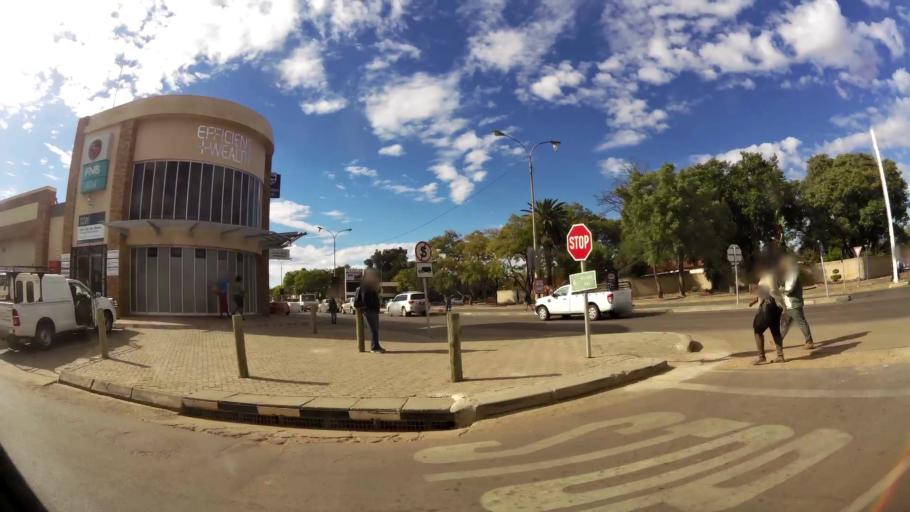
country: ZA
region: Limpopo
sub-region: Waterberg District Municipality
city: Bela-Bela
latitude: -24.8850
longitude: 28.2914
